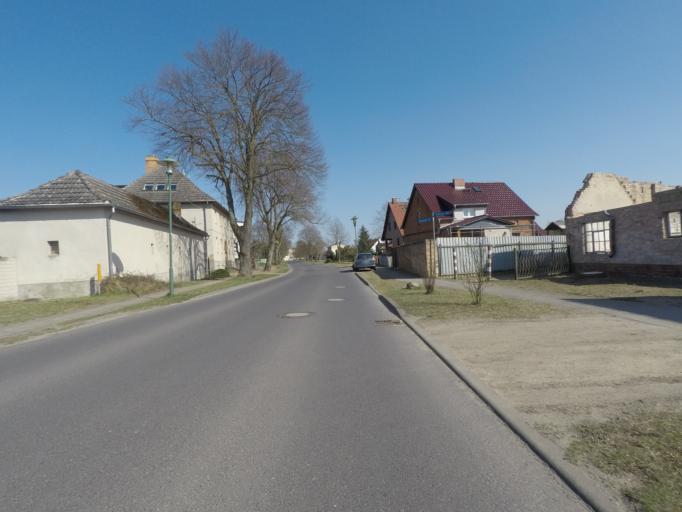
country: DE
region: Brandenburg
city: Britz
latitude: 52.8674
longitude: 13.7429
